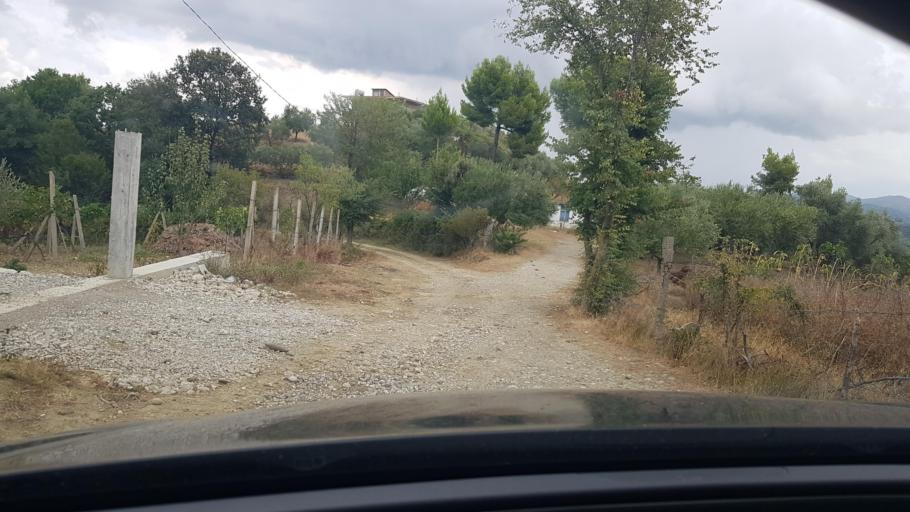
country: AL
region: Durres
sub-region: Rrethi i Durresit
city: Gjepalaj
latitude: 41.2990
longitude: 19.5557
